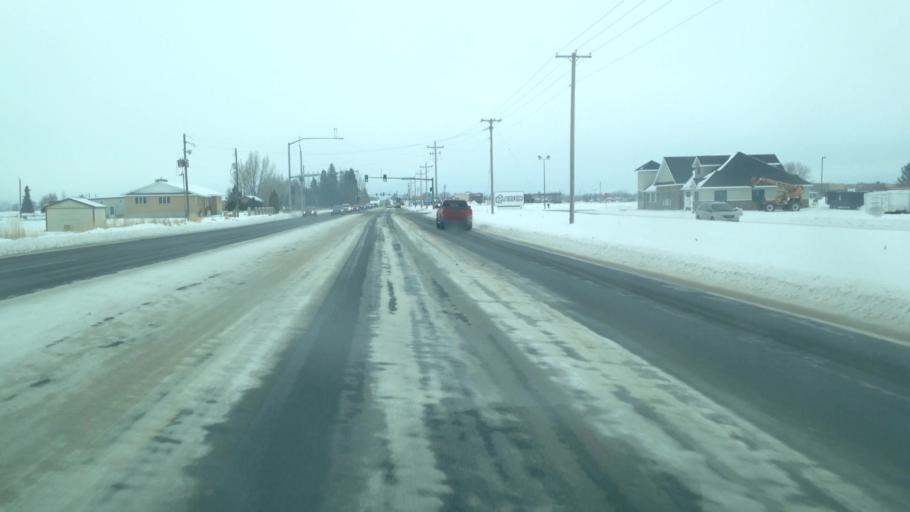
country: US
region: Idaho
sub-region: Madison County
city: Rexburg
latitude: 43.8503
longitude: -111.7779
